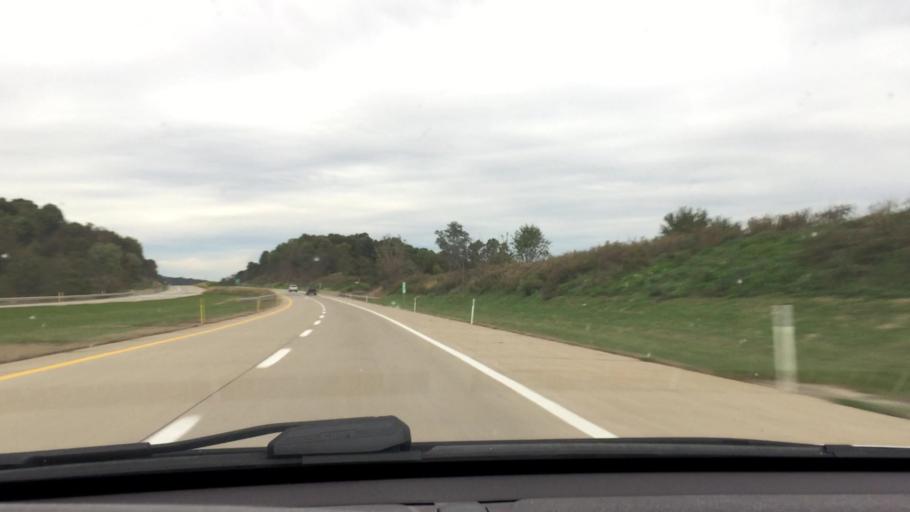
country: US
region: Pennsylvania
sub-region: Lawrence County
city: New Beaver
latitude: 40.8913
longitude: -80.3728
